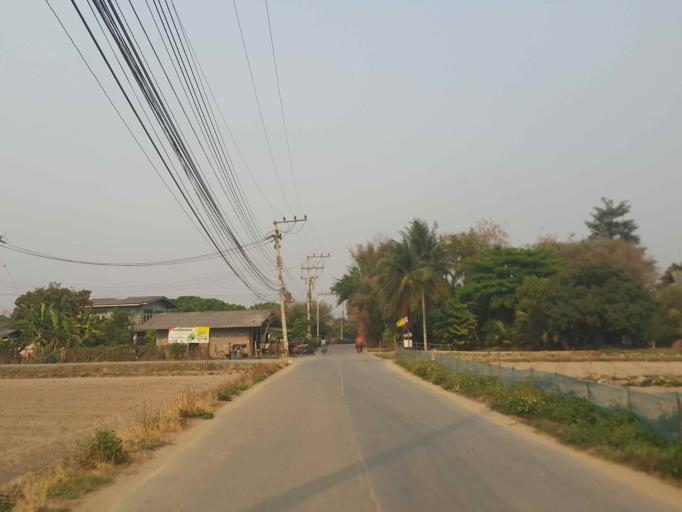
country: TH
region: Chiang Mai
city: San Sai
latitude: 18.9747
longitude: 98.9777
